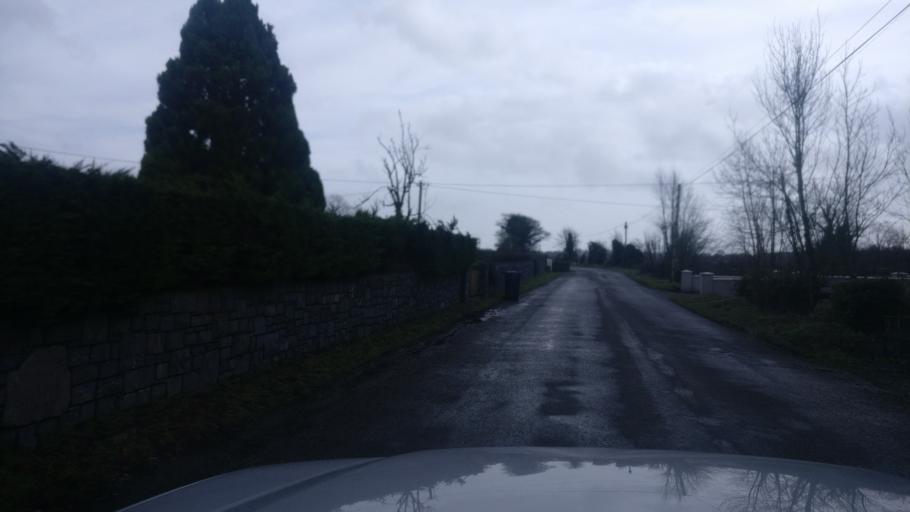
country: IE
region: Connaught
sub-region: County Galway
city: Loughrea
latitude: 53.2834
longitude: -8.4615
